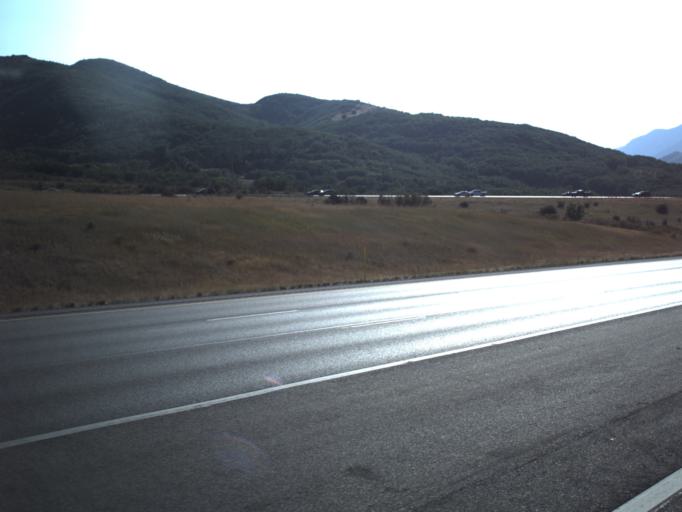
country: US
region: Utah
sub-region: Summit County
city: Summit Park
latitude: 40.7507
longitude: -111.7080
